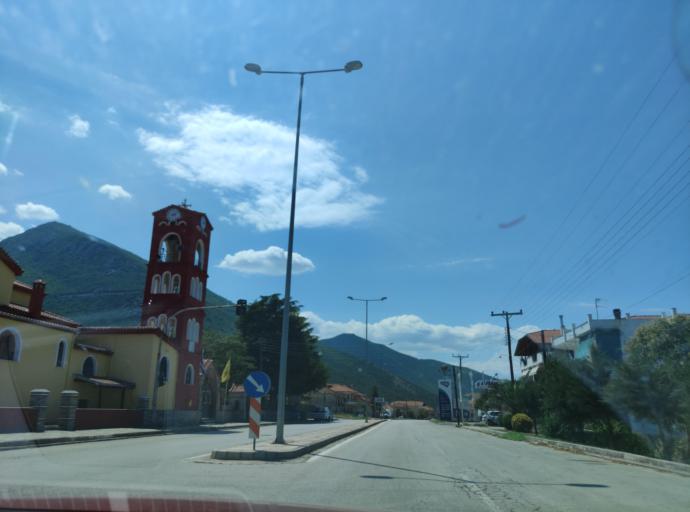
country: GR
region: East Macedonia and Thrace
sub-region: Nomos Kavalas
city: Nikisiani
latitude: 40.9713
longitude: 24.1481
